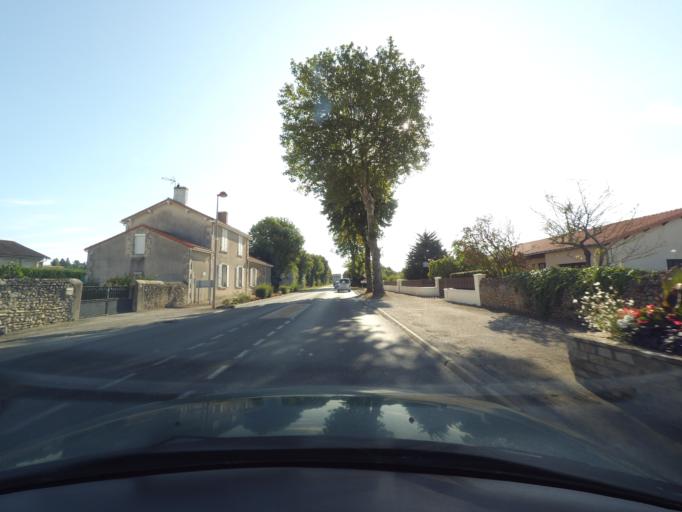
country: FR
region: Poitou-Charentes
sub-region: Departement des Deux-Sevres
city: Thenezay
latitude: 46.6551
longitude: -0.0730
